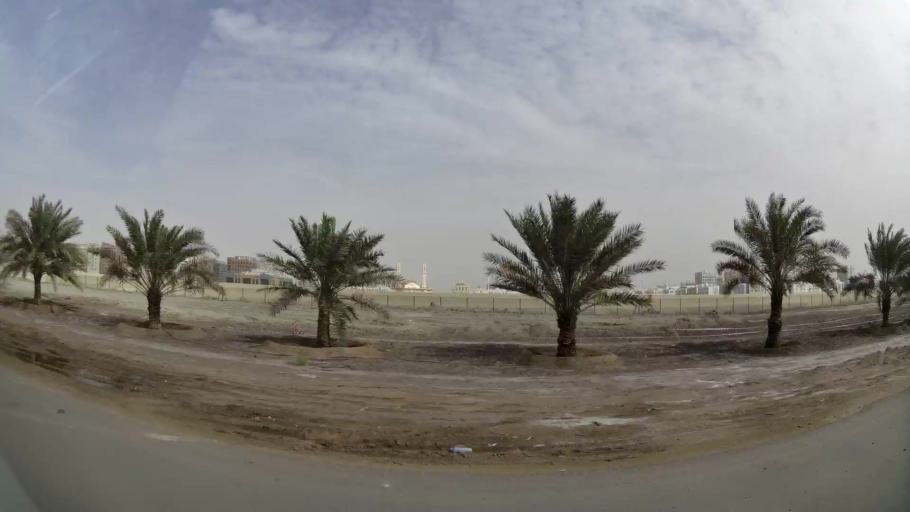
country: AE
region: Abu Dhabi
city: Abu Dhabi
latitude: 24.3308
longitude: 54.5271
